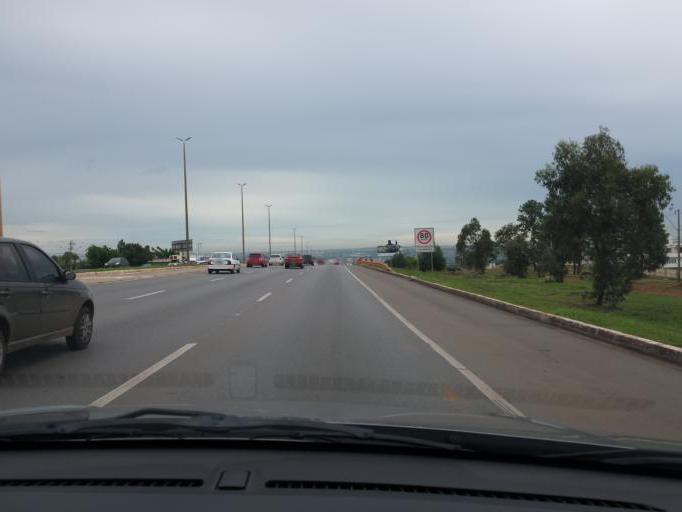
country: BR
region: Federal District
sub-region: Brasilia
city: Brasilia
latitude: -15.9000
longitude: -47.9627
